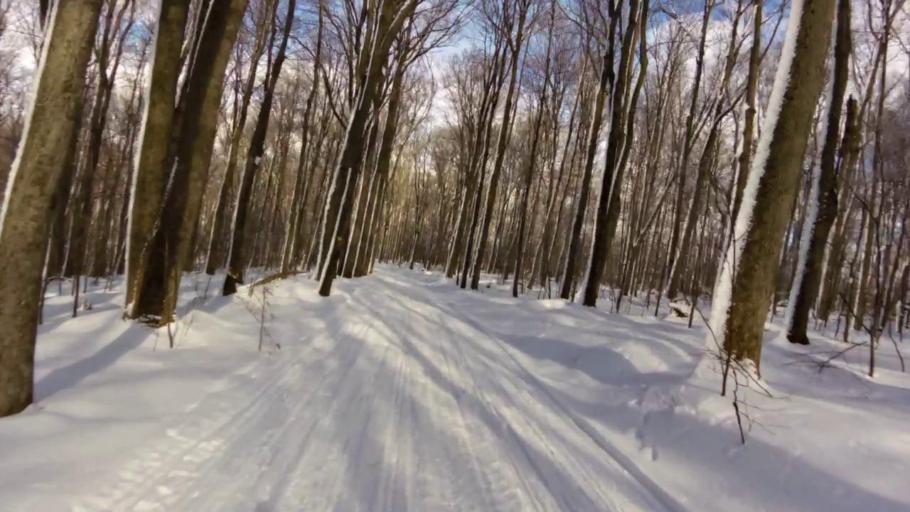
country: US
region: New York
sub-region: Cattaraugus County
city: Salamanca
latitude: 42.0658
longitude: -78.6947
